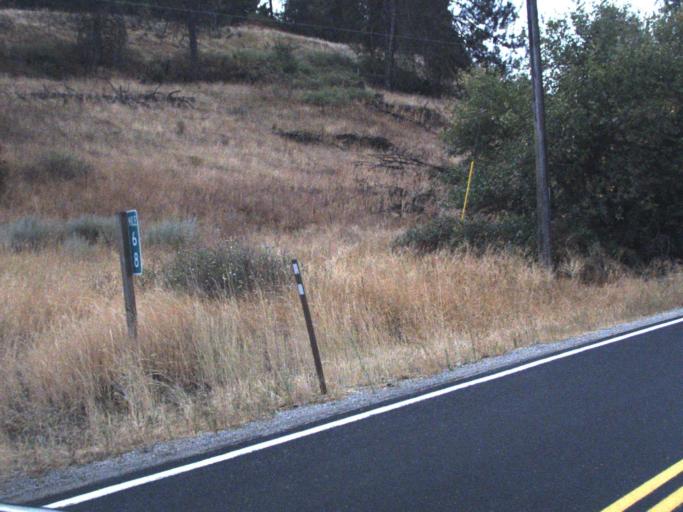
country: US
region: Washington
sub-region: Stevens County
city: Chewelah
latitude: 48.1251
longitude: -117.7446
